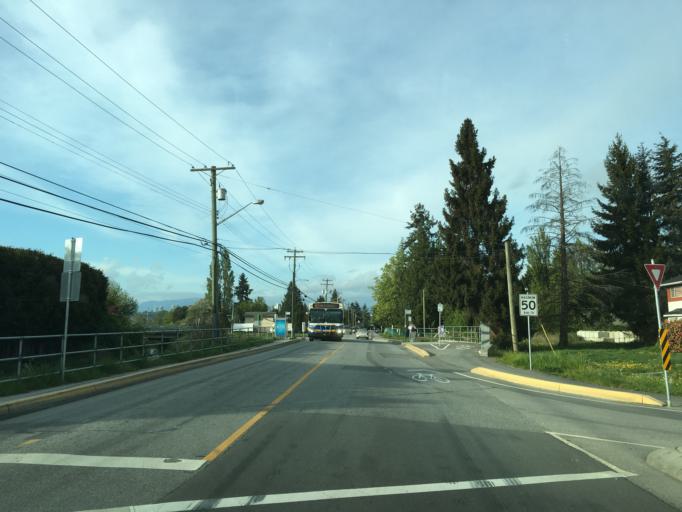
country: CA
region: British Columbia
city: New Westminster
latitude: 49.1770
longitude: -122.9686
